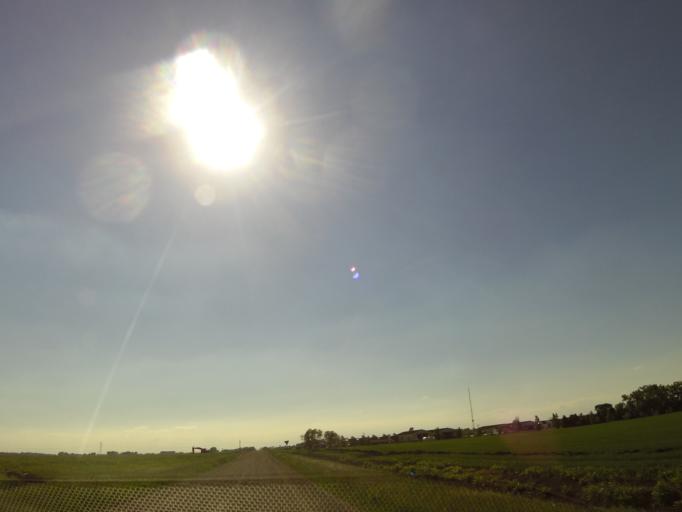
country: US
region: North Dakota
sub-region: Walsh County
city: Grafton
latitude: 48.3682
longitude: -97.2559
